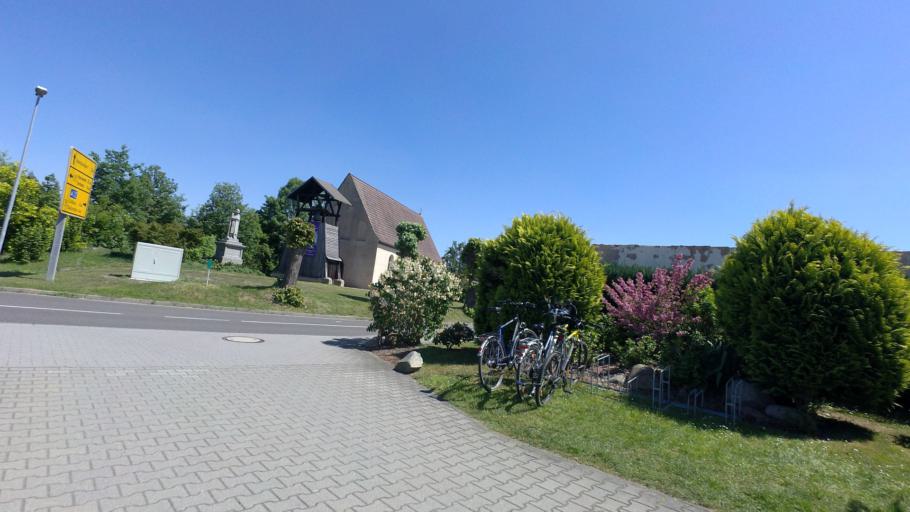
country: DE
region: Brandenburg
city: Cottbus
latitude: 51.6785
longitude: 14.3573
